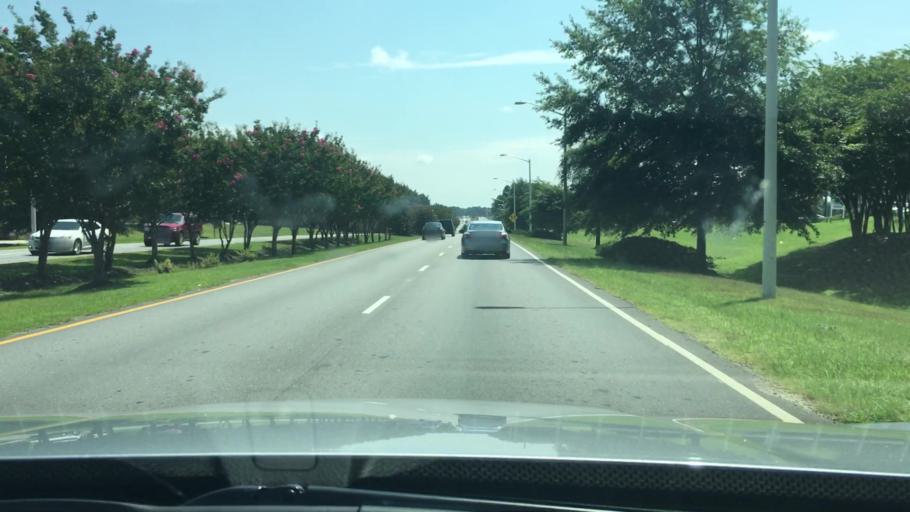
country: US
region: South Carolina
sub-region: Florence County
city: Florence
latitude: 34.1892
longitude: -79.8333
